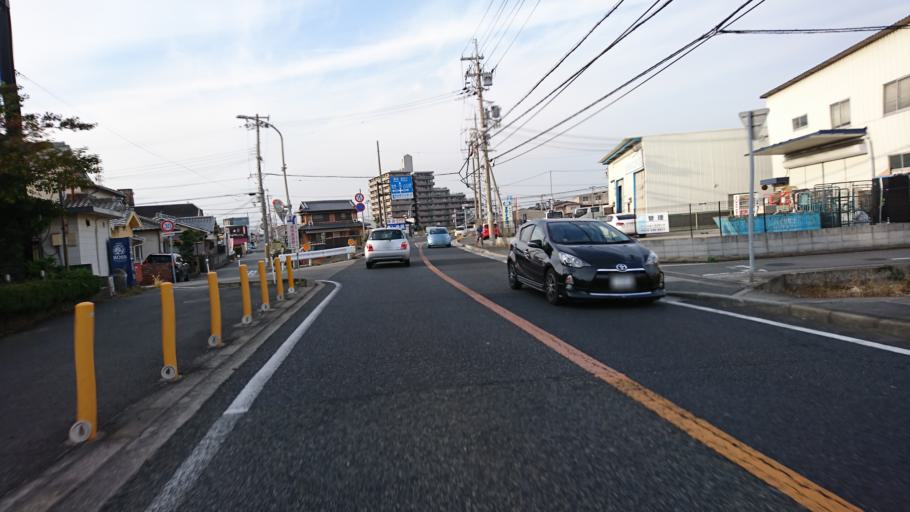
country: JP
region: Hyogo
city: Kakogawacho-honmachi
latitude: 34.7120
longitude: 134.8633
